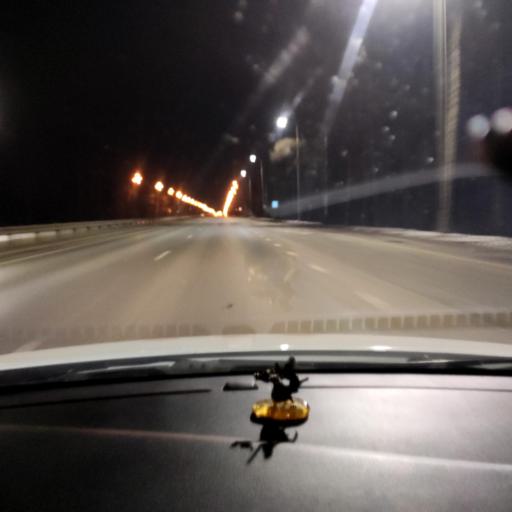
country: RU
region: Tatarstan
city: Osinovo
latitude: 55.8399
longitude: 48.8514
